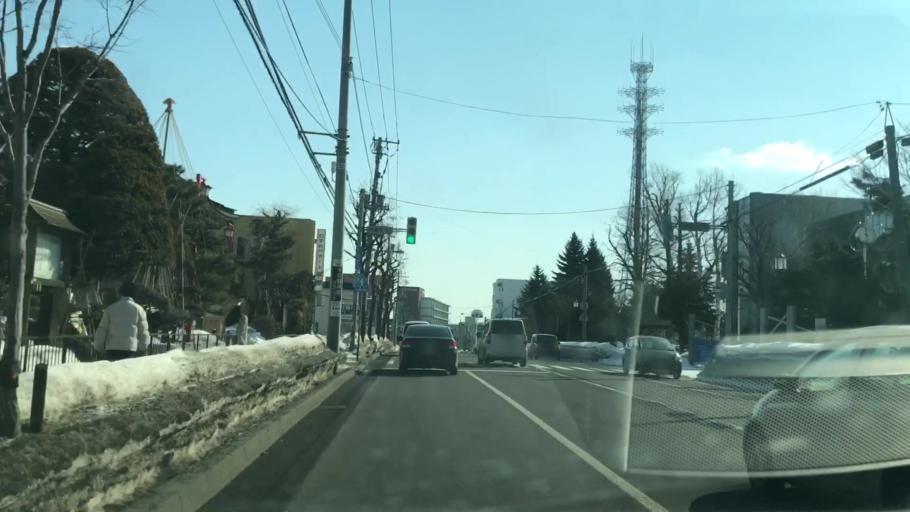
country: JP
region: Hokkaido
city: Sapporo
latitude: 43.0256
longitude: 141.3766
